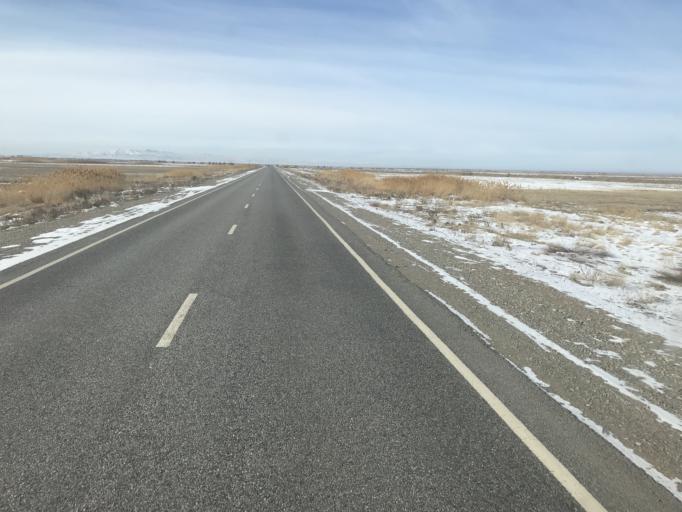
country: KZ
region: Zhambyl
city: Sarykemer
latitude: 43.0323
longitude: 71.3861
